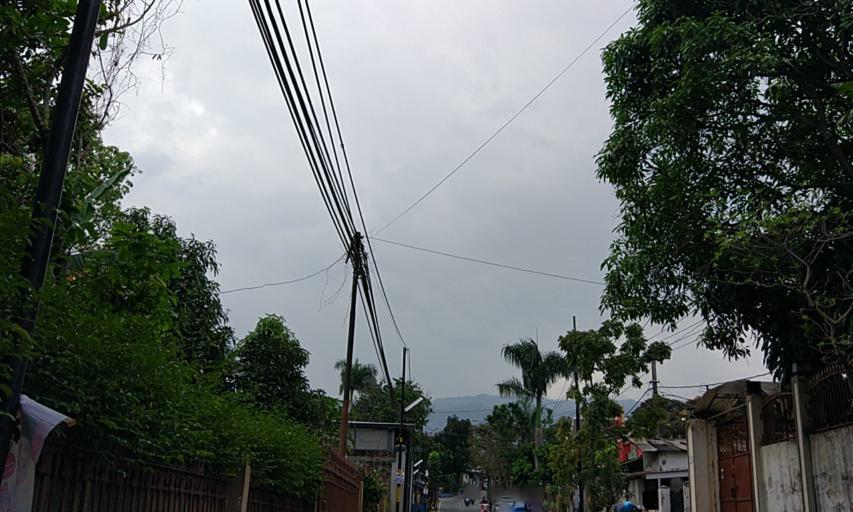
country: ID
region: West Java
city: Bandung
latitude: -6.8963
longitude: 107.6822
